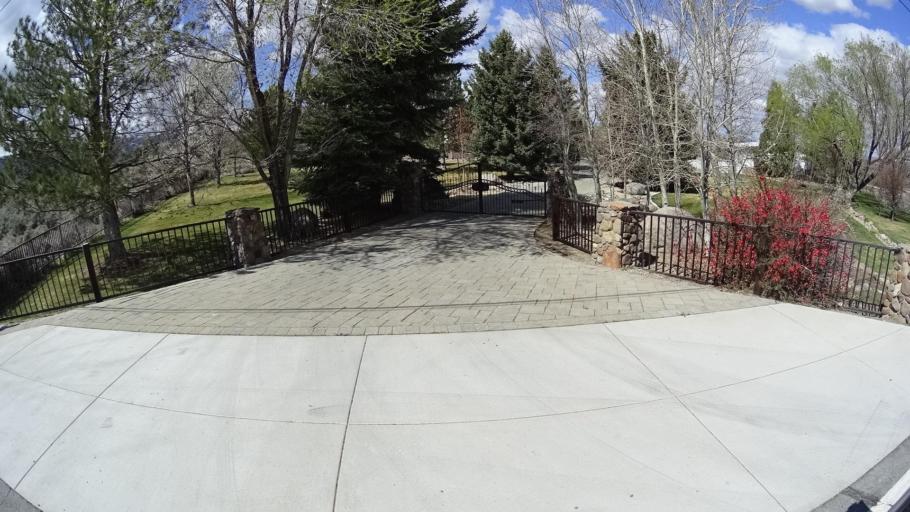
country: US
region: Nevada
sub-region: Washoe County
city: Reno
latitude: 39.4295
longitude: -119.7808
